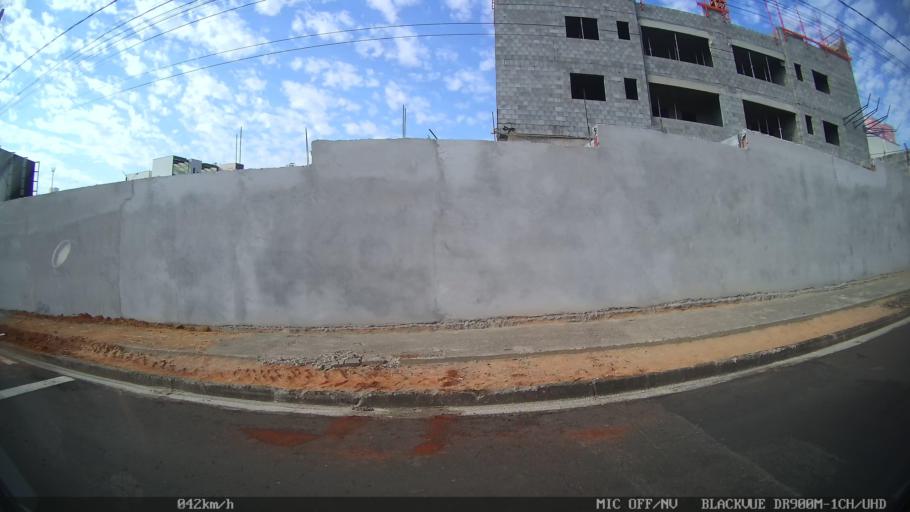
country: BR
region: Sao Paulo
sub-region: Americana
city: Americana
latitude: -22.7375
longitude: -47.3488
